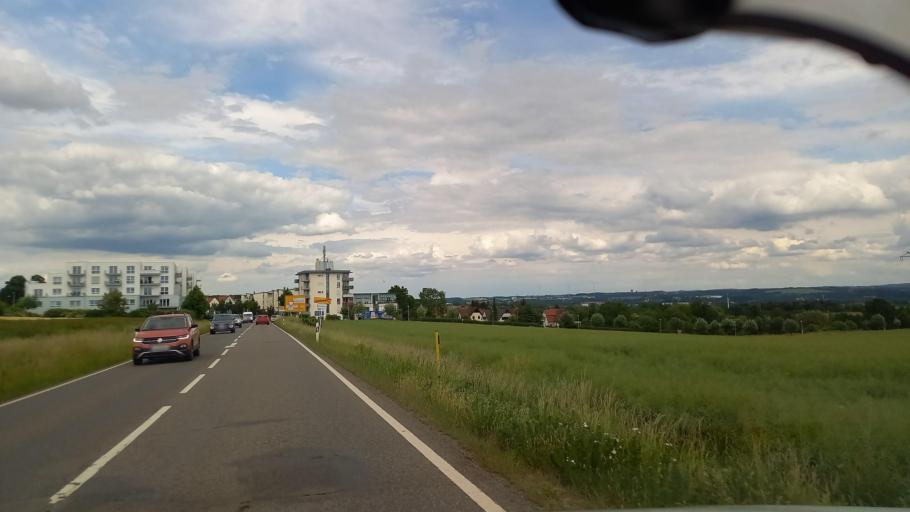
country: DE
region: Saxony
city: Lichtentanne
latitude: 50.7155
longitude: 12.4305
